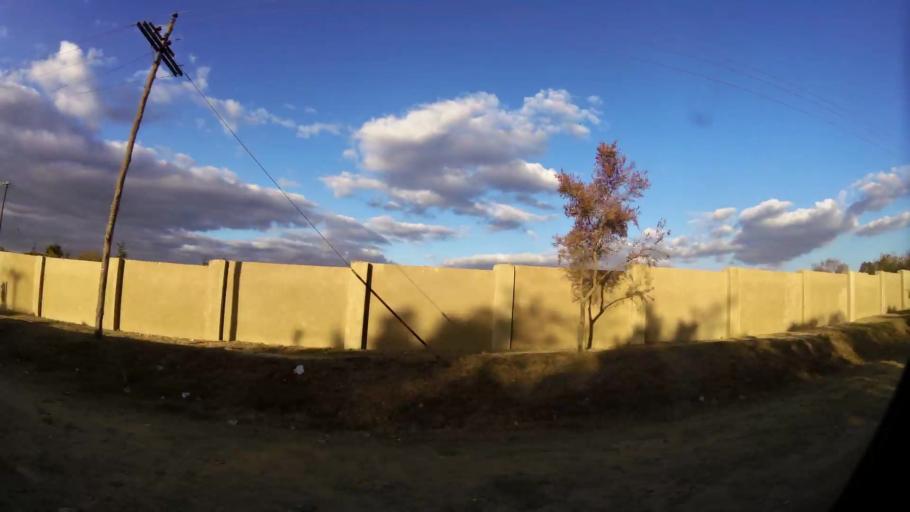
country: ZA
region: Gauteng
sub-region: City of Johannesburg Metropolitan Municipality
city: Midrand
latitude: -25.9672
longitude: 28.1536
